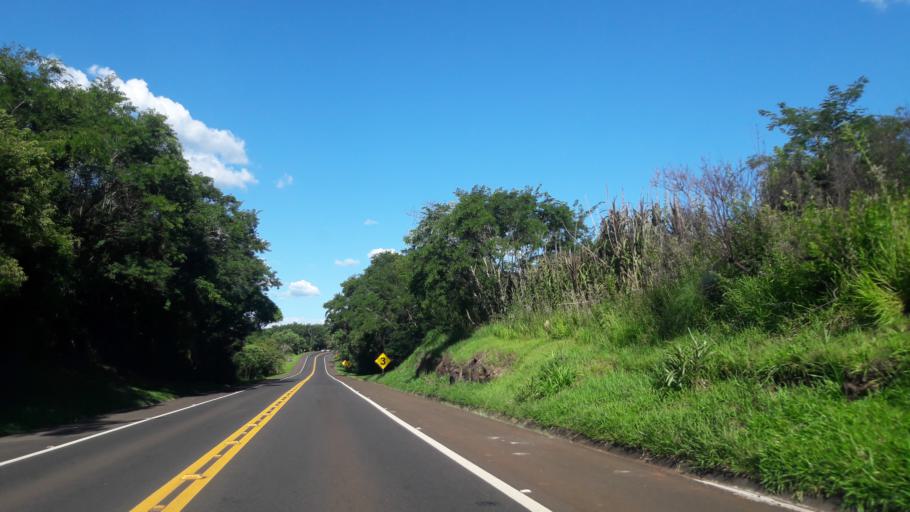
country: BR
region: Parana
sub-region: Laranjeiras Do Sul
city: Laranjeiras do Sul
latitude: -25.4203
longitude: -52.0379
